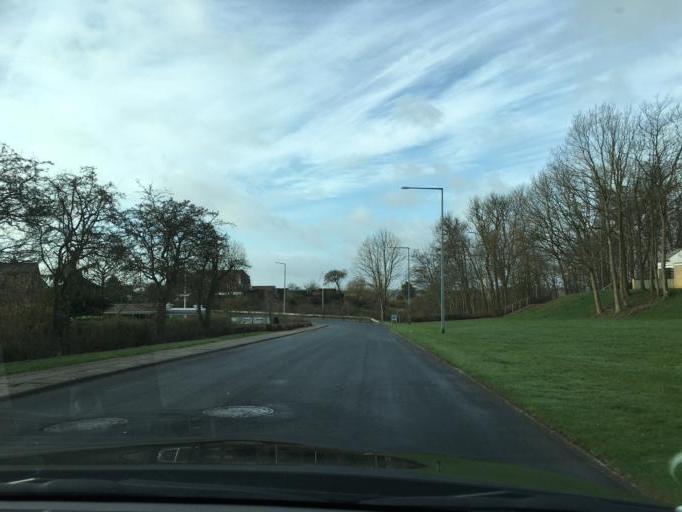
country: DK
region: South Denmark
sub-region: Kolding Kommune
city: Kolding
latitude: 55.5008
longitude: 9.4488
